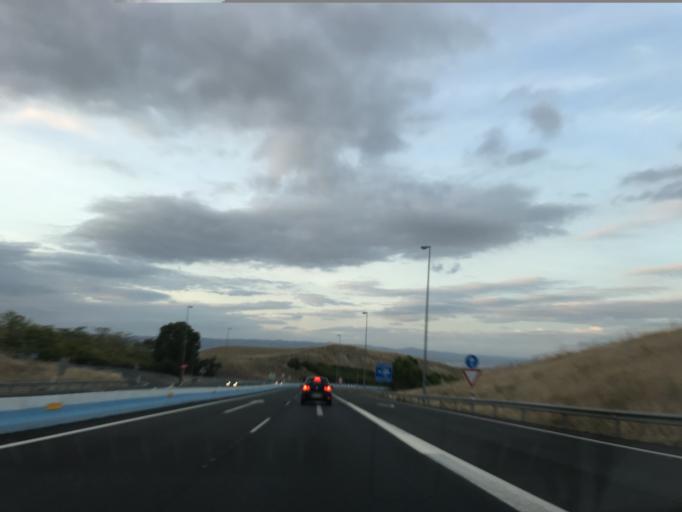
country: ES
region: Andalusia
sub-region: Province of Cordoba
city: La Victoria
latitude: 37.7632
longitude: -4.8224
